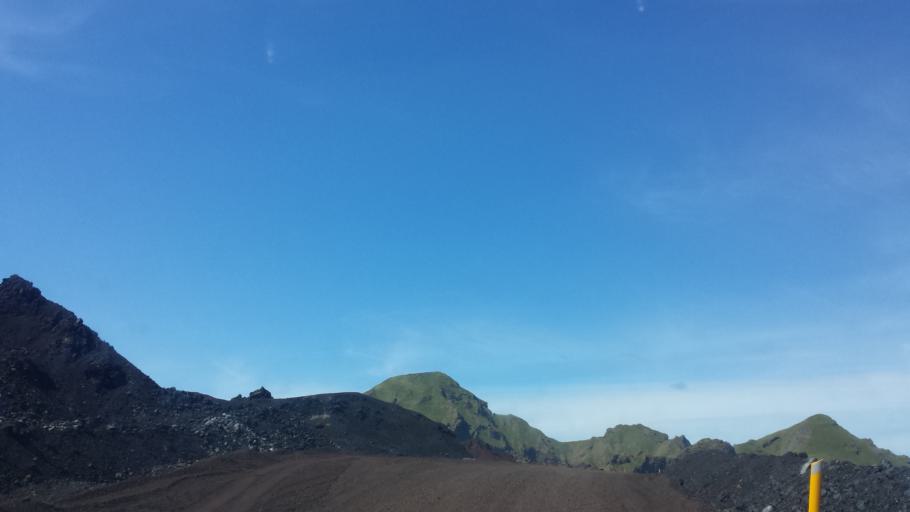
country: IS
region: South
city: Vestmannaeyjar
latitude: 63.4392
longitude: -20.2315
